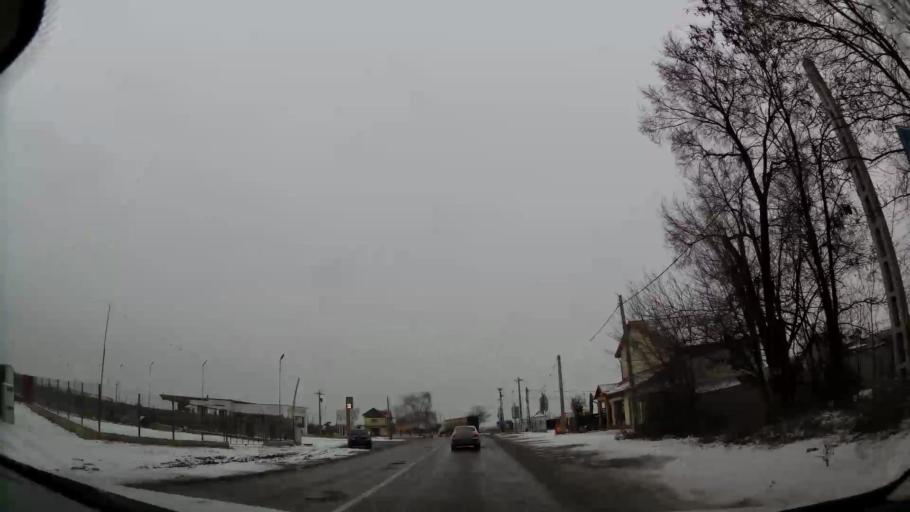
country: RO
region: Dambovita
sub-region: Comuna Ulmi
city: Ulmi
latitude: 44.8958
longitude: 25.5093
